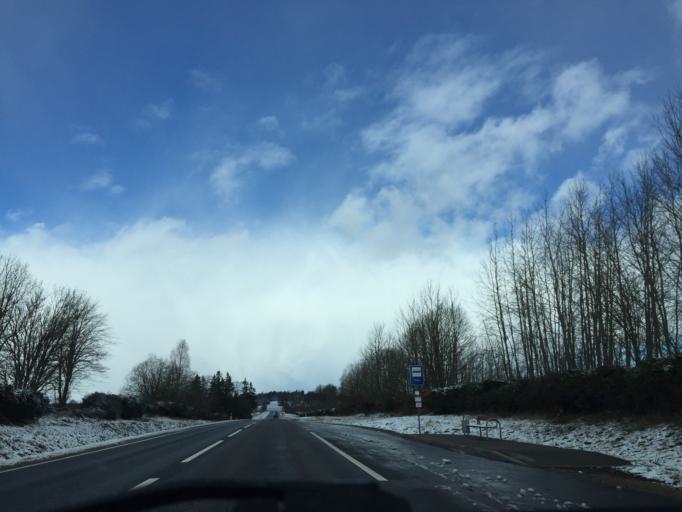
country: LV
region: Kandava
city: Kandava
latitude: 57.1320
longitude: 22.7369
